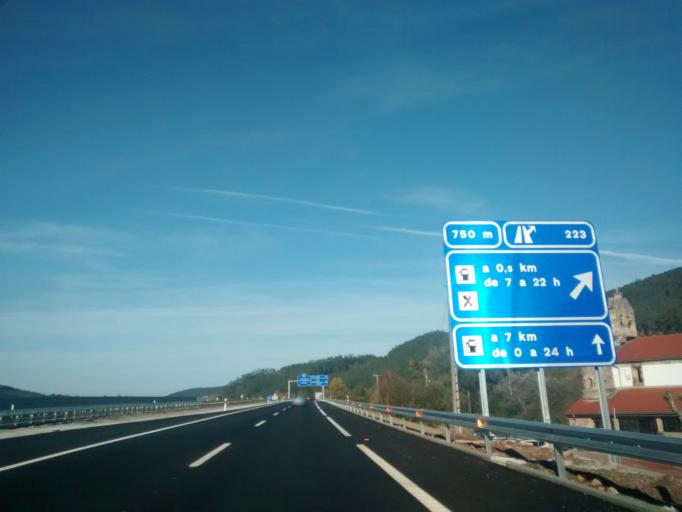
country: ES
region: Cantabria
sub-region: Provincia de Cantabria
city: Puente Viesgo
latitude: 43.3259
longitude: -3.9593
